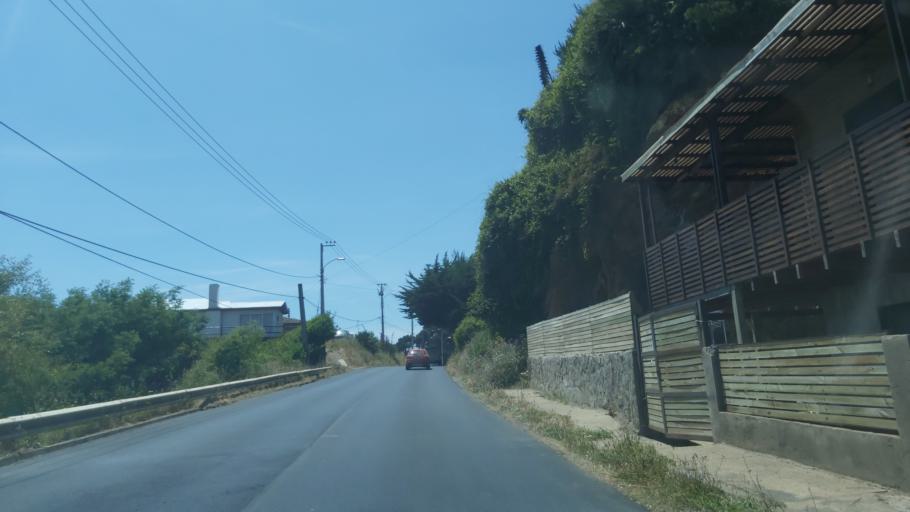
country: CL
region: Maule
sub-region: Provincia de Cauquenes
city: Cauquenes
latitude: -35.8190
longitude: -72.5952
